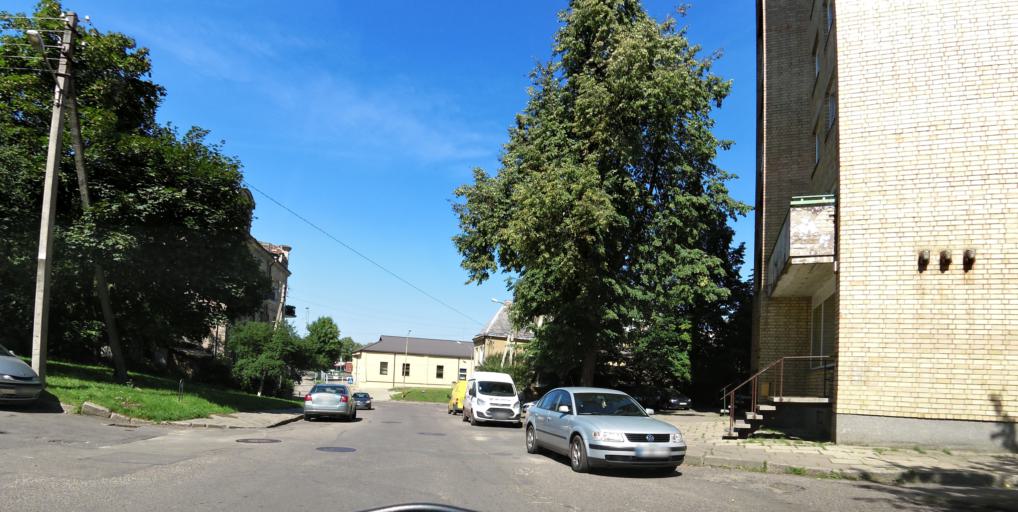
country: LT
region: Vilnius County
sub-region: Vilnius
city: Vilnius
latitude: 54.6699
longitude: 25.2892
